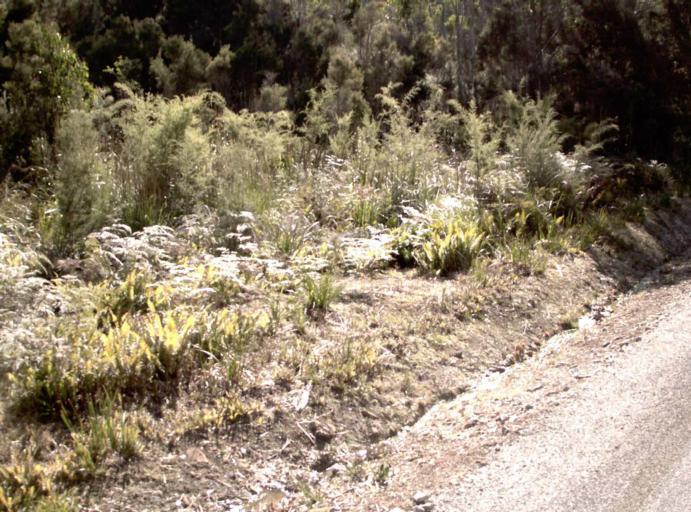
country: AU
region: Tasmania
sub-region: Launceston
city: Mayfield
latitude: -41.3099
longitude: 147.1988
